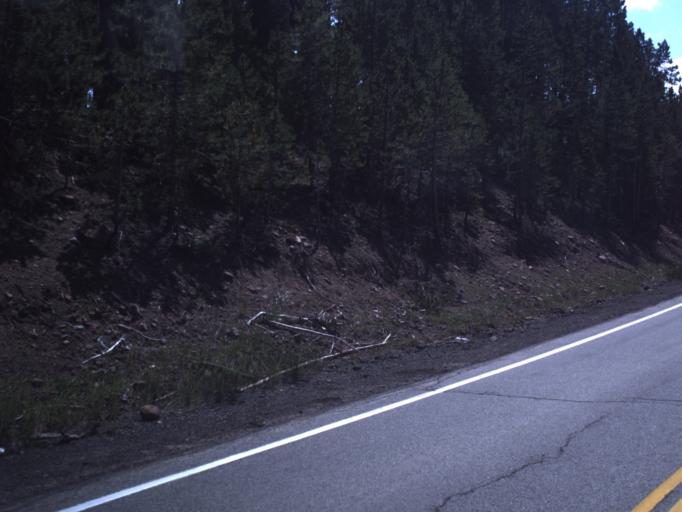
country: US
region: Utah
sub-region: Uintah County
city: Maeser
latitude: 40.7590
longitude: -109.4710
